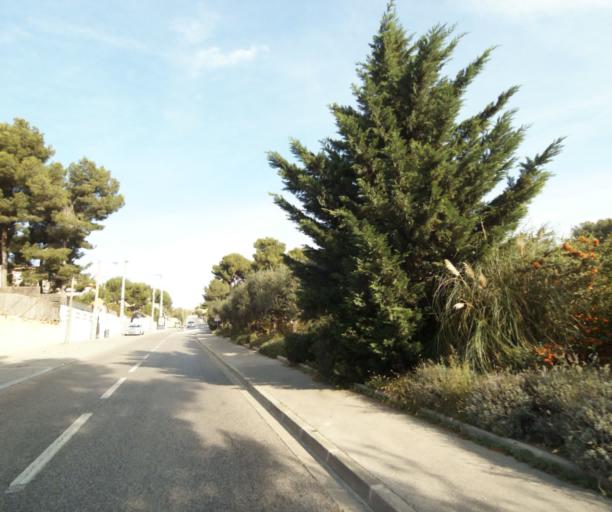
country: FR
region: Provence-Alpes-Cote d'Azur
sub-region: Departement des Bouches-du-Rhone
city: Carry-le-Rouet
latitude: 43.3321
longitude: 5.1589
